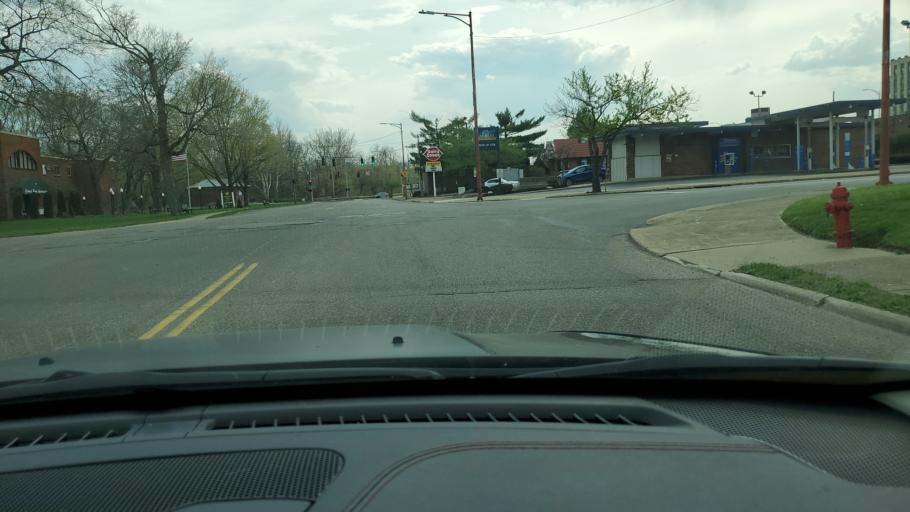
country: US
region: Ohio
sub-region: Trumbull County
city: Niles
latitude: 41.1818
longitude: -80.7635
